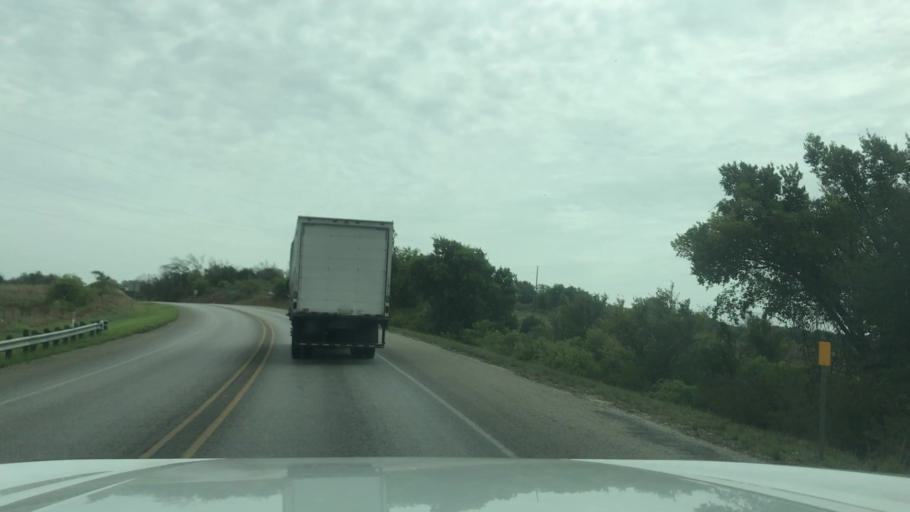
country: US
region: Texas
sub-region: Erath County
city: Dublin
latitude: 32.0874
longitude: -98.4312
